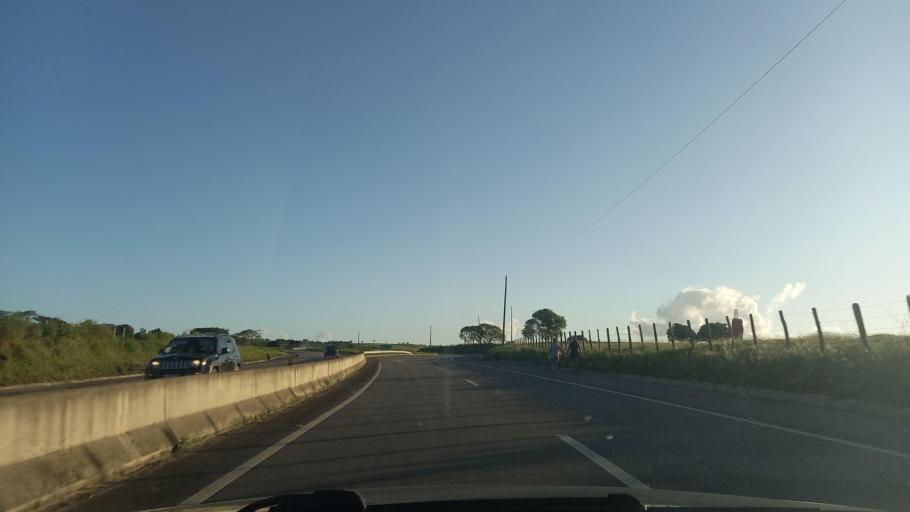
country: BR
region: Alagoas
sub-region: Limoeiro De Anadia
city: Limoeiro de Anadia
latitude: -9.7430
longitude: -36.4994
